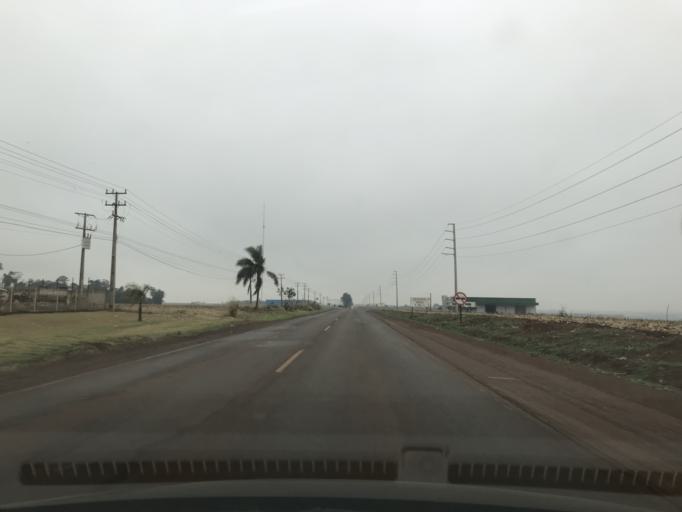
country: BR
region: Parana
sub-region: Palotina
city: Palotina
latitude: -24.3134
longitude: -53.8332
